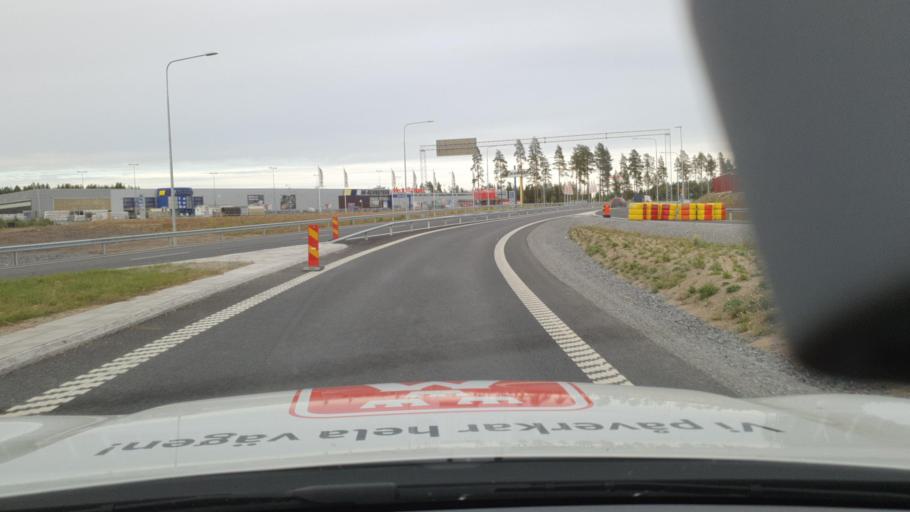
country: SE
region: Vaesterbotten
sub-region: Umea Kommun
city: Roback
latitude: 63.8459
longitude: 20.1495
